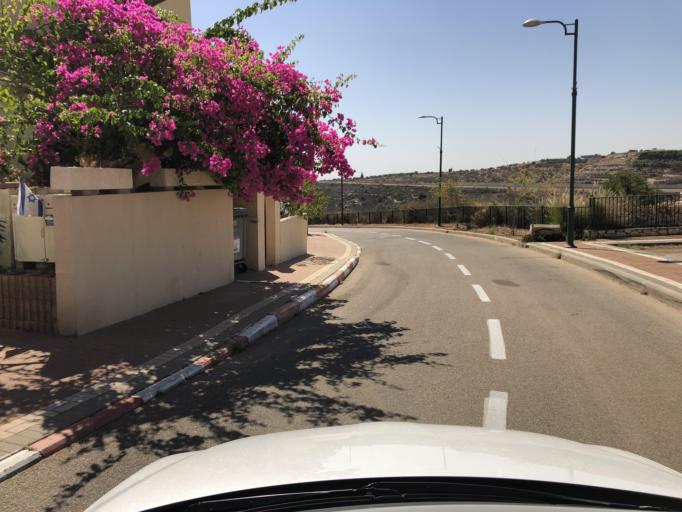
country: PS
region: West Bank
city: An Nabi Ilyas
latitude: 32.1672
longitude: 35.0162
